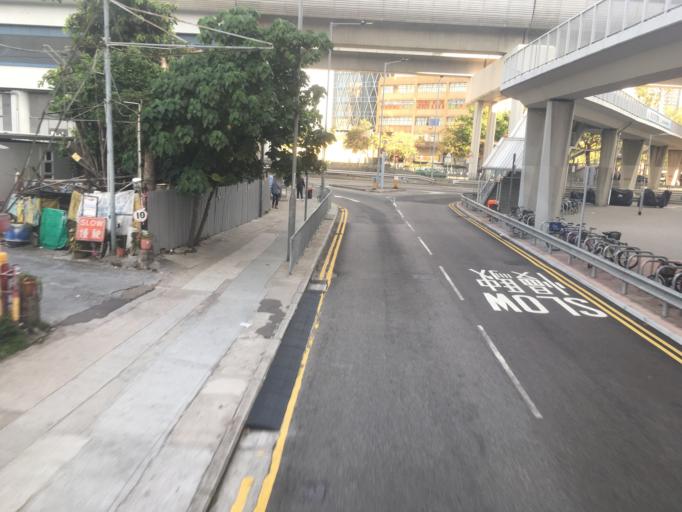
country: HK
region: Yuen Long
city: Yuen Long Kau Hui
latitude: 22.4462
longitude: 114.0274
